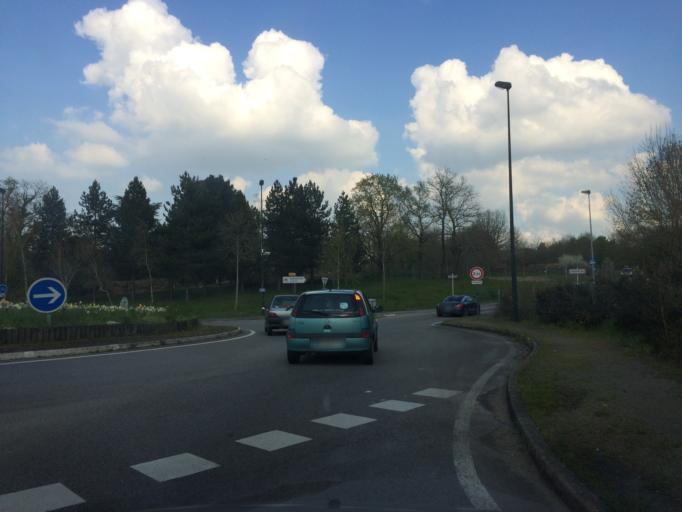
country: FR
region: Pays de la Loire
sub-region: Departement de la Loire-Atlantique
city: Carquefou
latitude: 47.2911
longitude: -1.5012
